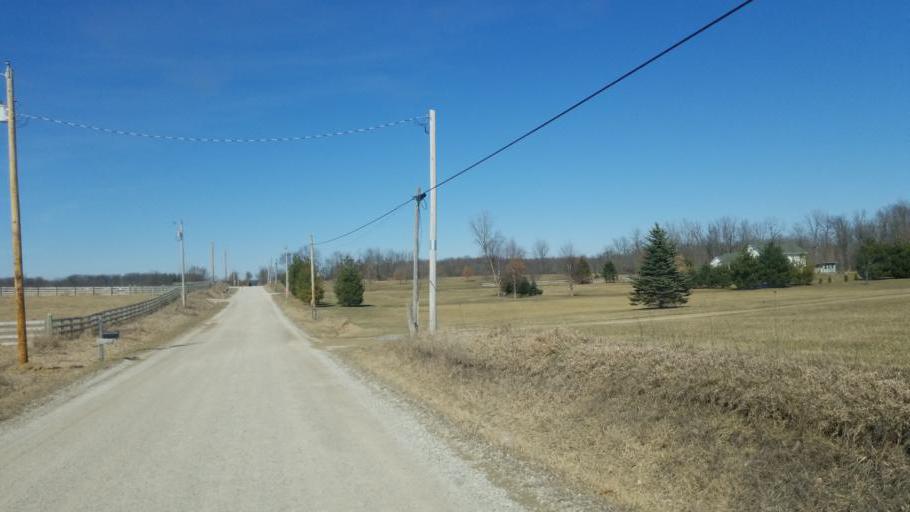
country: US
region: Ohio
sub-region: Morrow County
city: Mount Gilead
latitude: 40.5828
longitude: -82.7909
